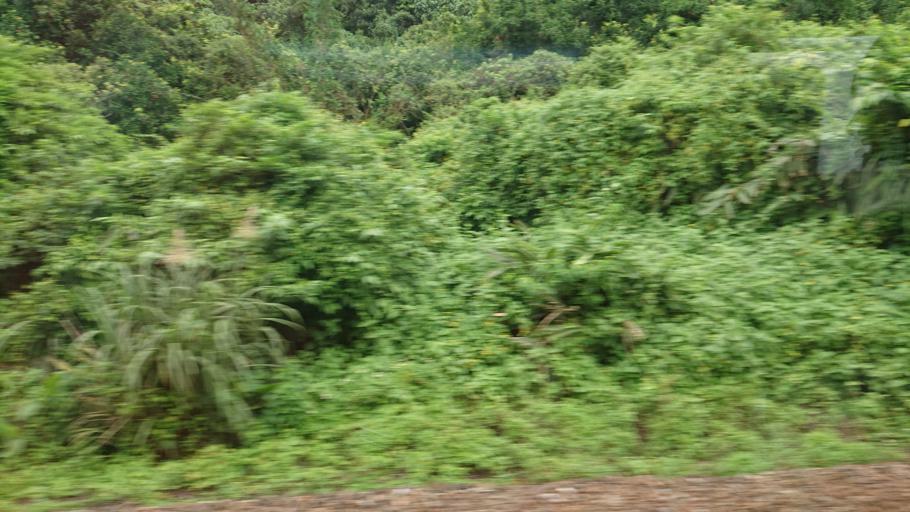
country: TW
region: Taiwan
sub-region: Yilan
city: Yilan
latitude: 24.9122
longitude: 121.8769
